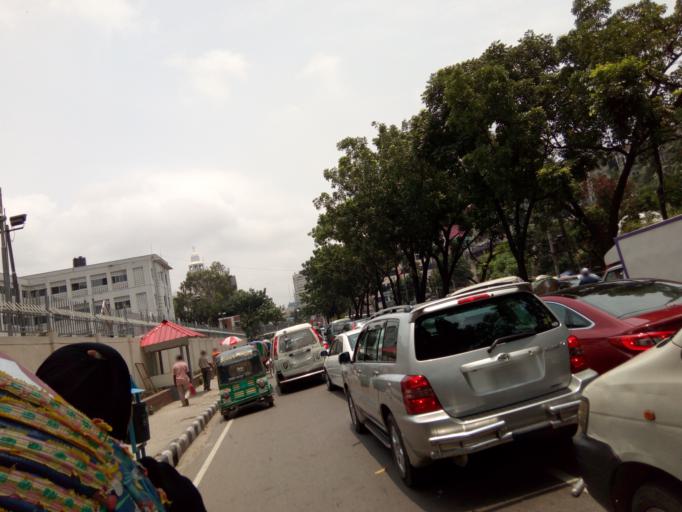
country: BD
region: Dhaka
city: Paltan
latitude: 23.7279
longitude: 90.4094
